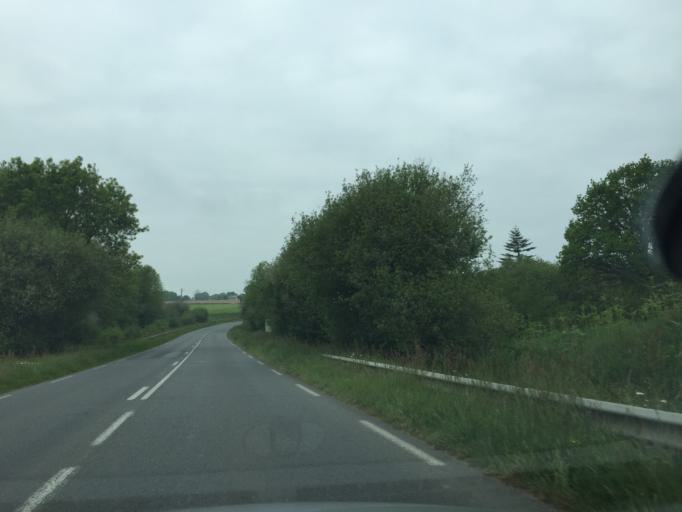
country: FR
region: Brittany
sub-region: Departement des Cotes-d'Armor
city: Saint-Cast-le-Guildo
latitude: 48.5866
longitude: -2.2404
